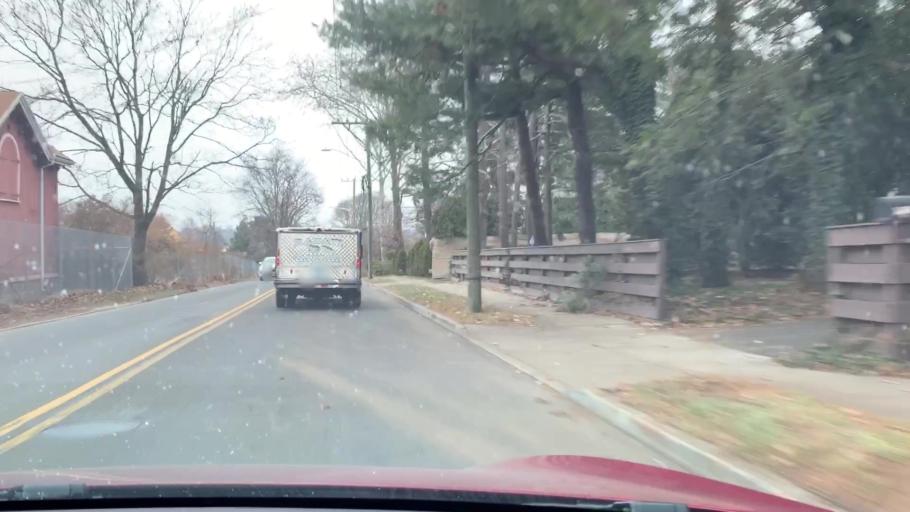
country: US
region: Connecticut
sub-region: Fairfield County
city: Stamford
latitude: 41.0677
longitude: -73.5352
